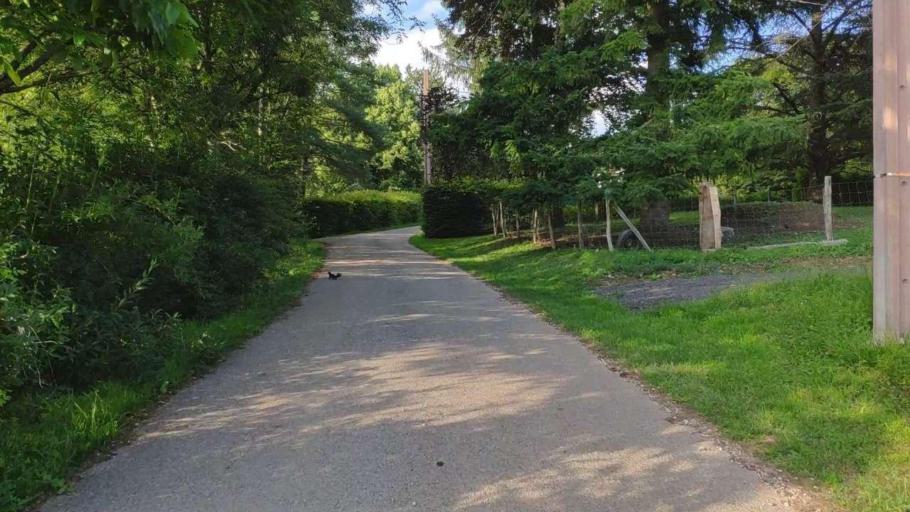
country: FR
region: Franche-Comte
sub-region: Departement du Jura
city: Bletterans
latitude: 46.7658
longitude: 5.5406
